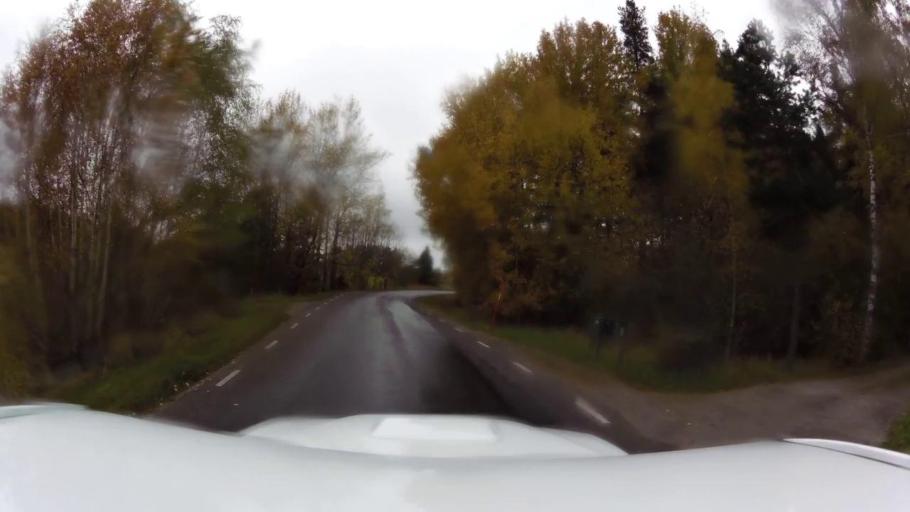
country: SE
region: OEstergoetland
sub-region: Linkopings Kommun
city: Linghem
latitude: 58.4630
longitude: 15.8267
